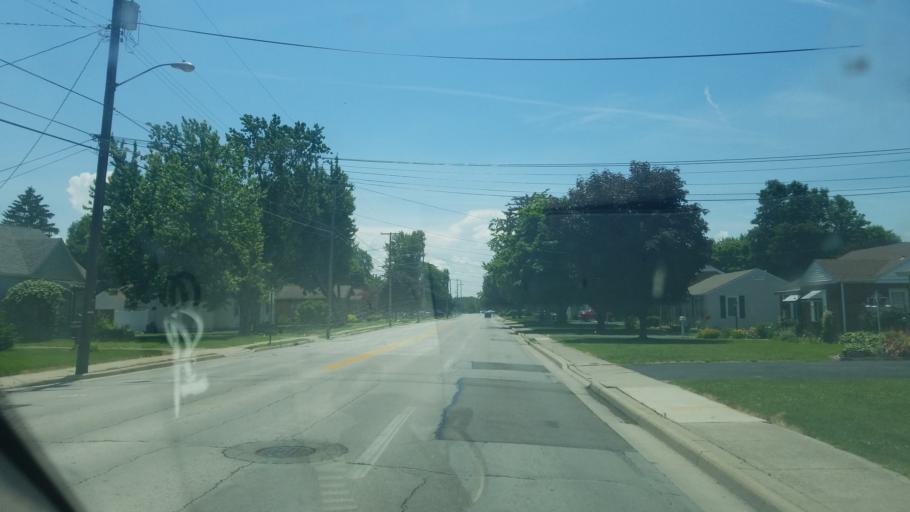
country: US
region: Ohio
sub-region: Hancock County
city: Findlay
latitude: 41.0251
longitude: -83.6412
